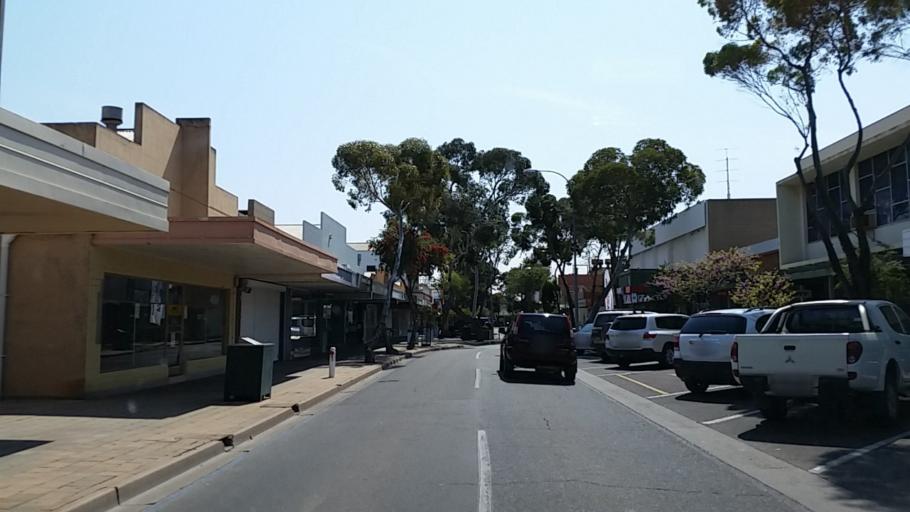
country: AU
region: South Australia
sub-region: Port Augusta
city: Port Augusta West
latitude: -32.4935
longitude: 137.7636
